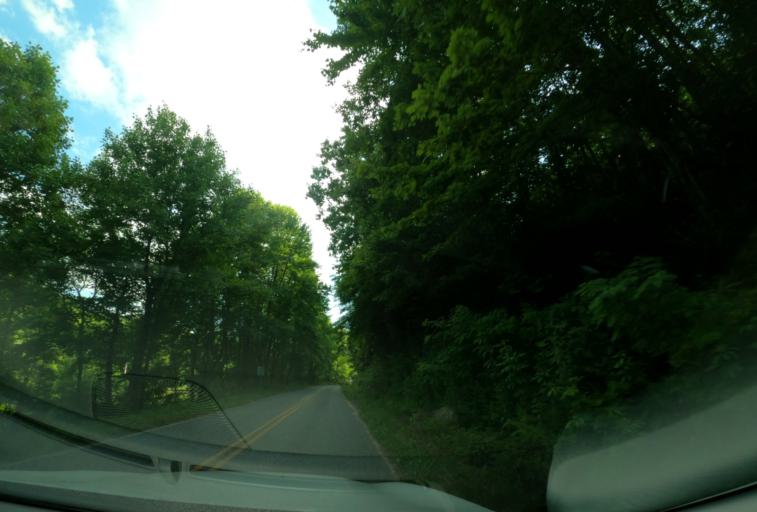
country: US
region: North Carolina
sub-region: Transylvania County
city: Brevard
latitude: 35.2437
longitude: -82.8582
